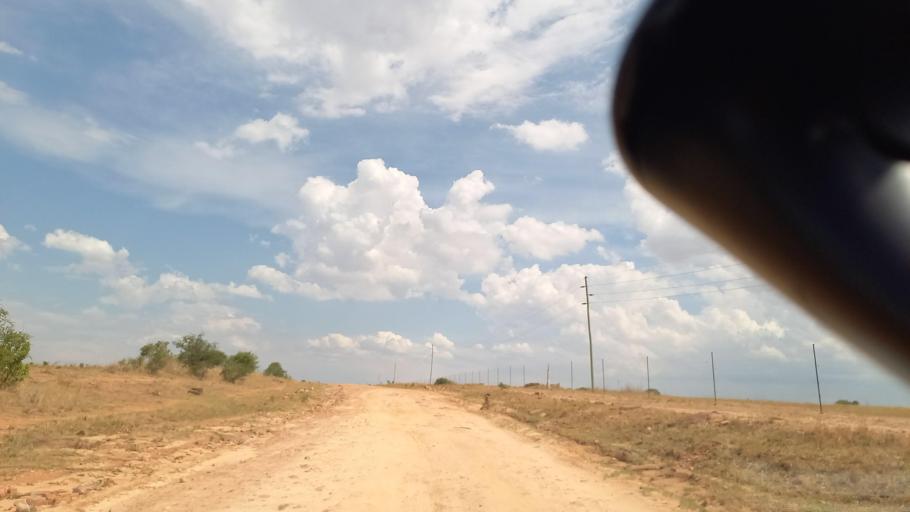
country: ZM
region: Southern
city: Nakambala
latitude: -16.1059
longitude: 28.0220
